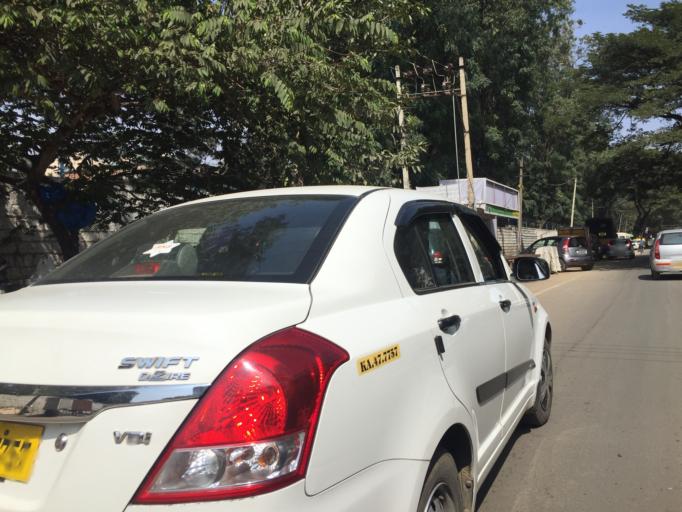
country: IN
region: Karnataka
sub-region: Bangalore Urban
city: Bangalore
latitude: 12.9570
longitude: 77.6537
